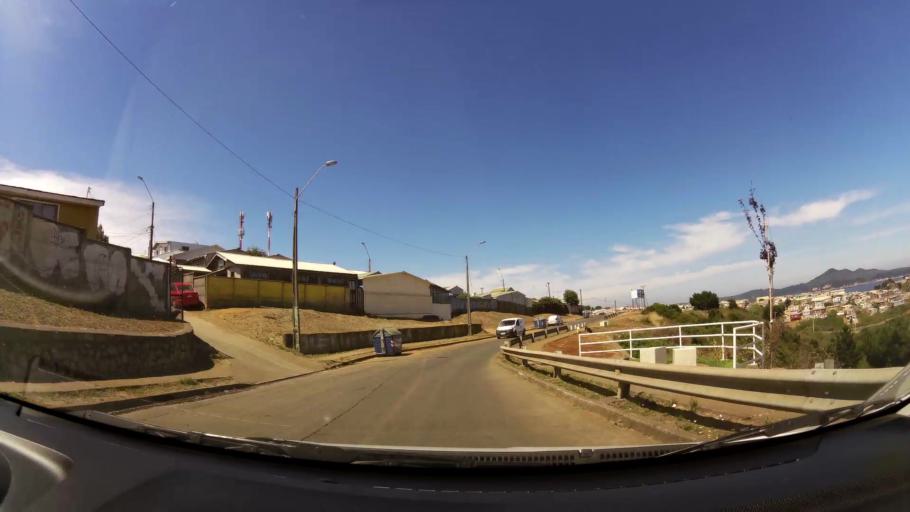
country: CL
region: Biobio
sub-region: Provincia de Concepcion
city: Talcahuano
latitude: -36.7157
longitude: -73.1411
